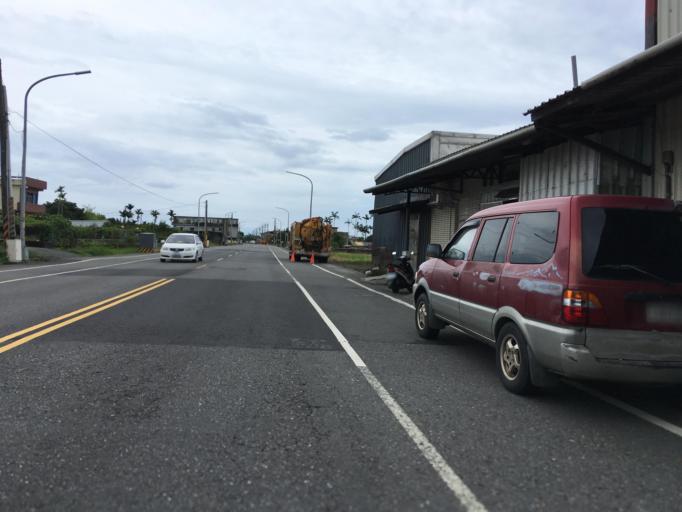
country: TW
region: Taiwan
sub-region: Yilan
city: Yilan
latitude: 24.6865
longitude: 121.8013
